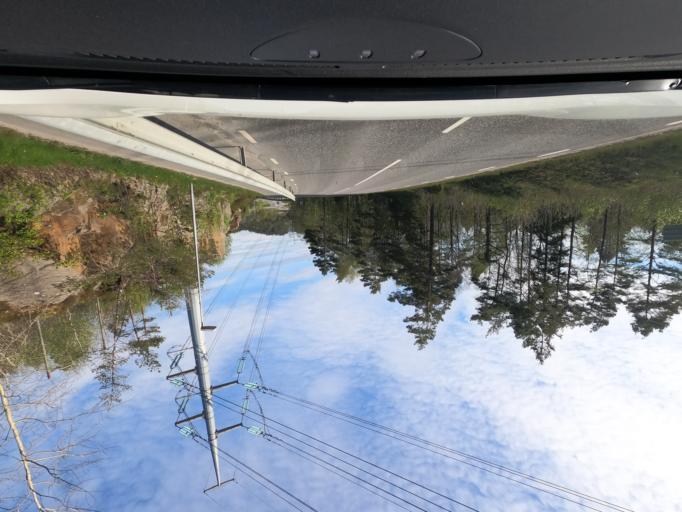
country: SE
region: Vaestra Goetaland
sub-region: Harryda Kommun
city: Landvetter
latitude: 57.6790
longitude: 12.2407
